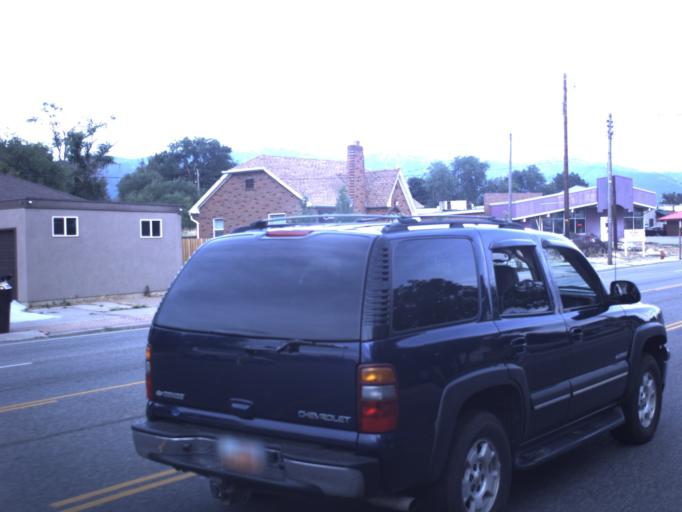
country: US
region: Utah
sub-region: Davis County
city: Clearfield
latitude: 41.1100
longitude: -112.0226
